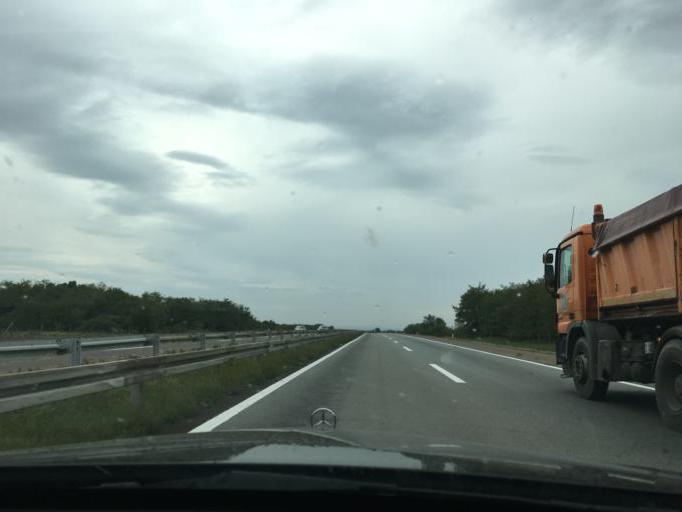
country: RS
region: Central Serbia
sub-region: Pomoravski Okrug
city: Cuprija
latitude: 43.9074
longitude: 21.3931
